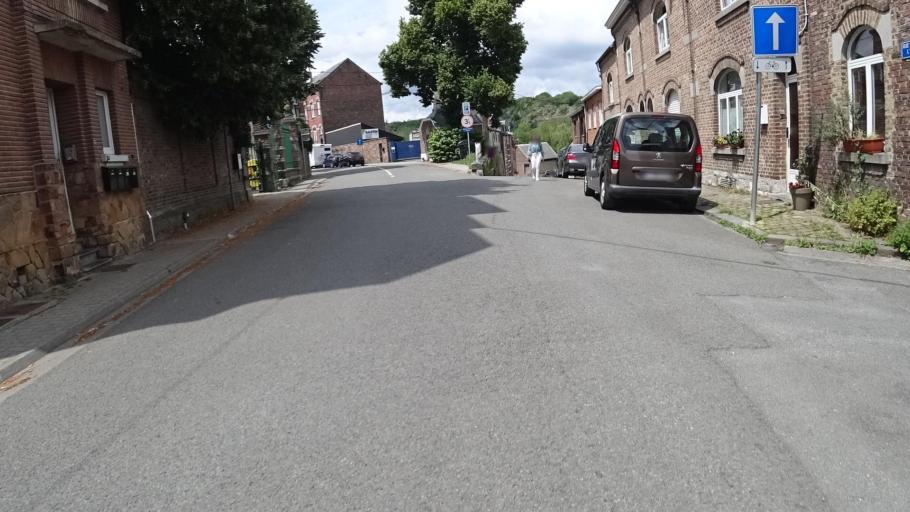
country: BE
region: Wallonia
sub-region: Province de Namur
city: Namur
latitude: 50.4731
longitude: 4.8554
